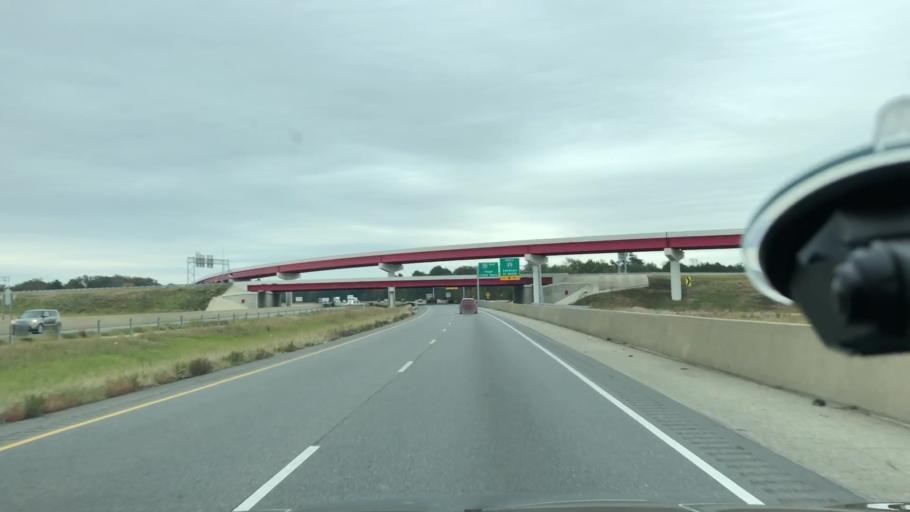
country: US
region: Arkansas
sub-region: Miller County
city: Texarkana
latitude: 33.4792
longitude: -93.9890
